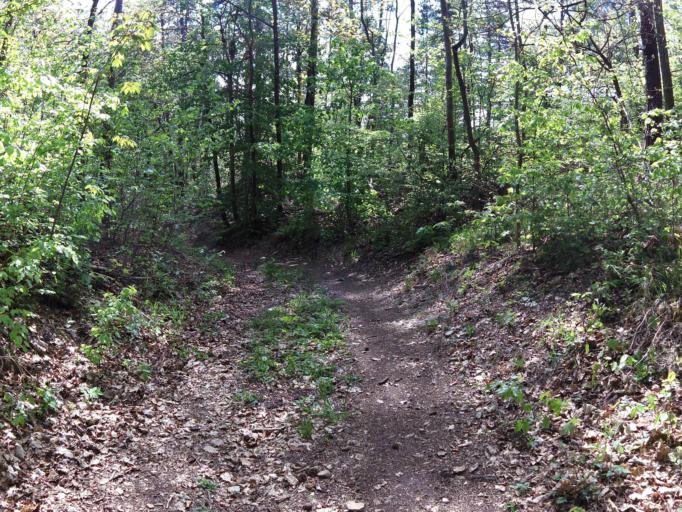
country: DE
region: Thuringia
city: Eisenach
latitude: 50.9705
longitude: 10.3589
